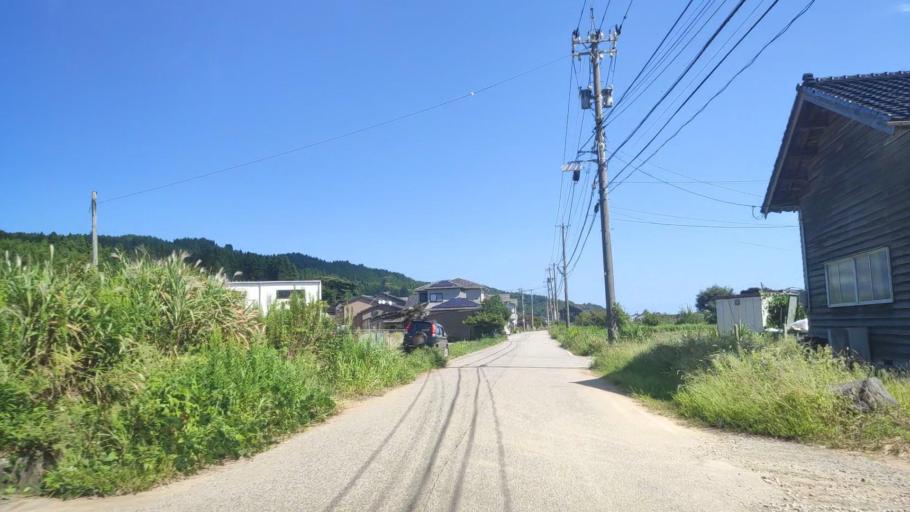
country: JP
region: Ishikawa
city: Nanao
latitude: 37.3739
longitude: 136.8749
